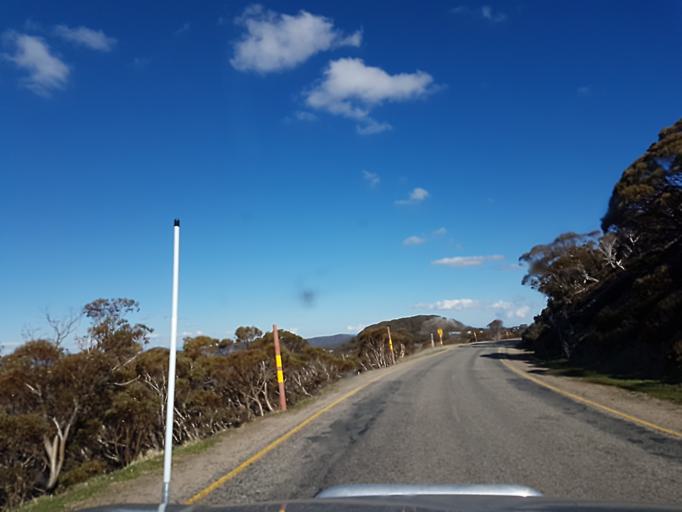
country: AU
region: Victoria
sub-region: Alpine
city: Mount Beauty
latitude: -36.9849
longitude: 147.1465
